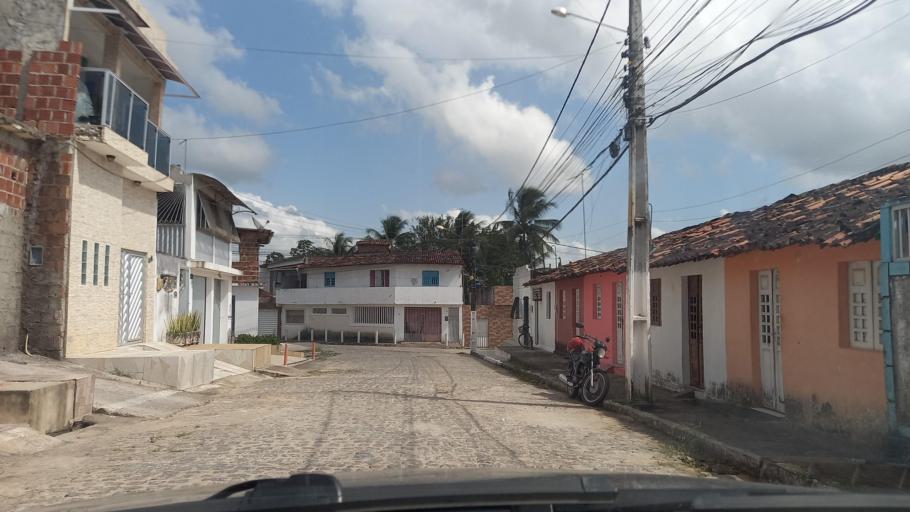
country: BR
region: Pernambuco
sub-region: Goiana
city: Goiana
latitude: -7.5654
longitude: -34.9960
